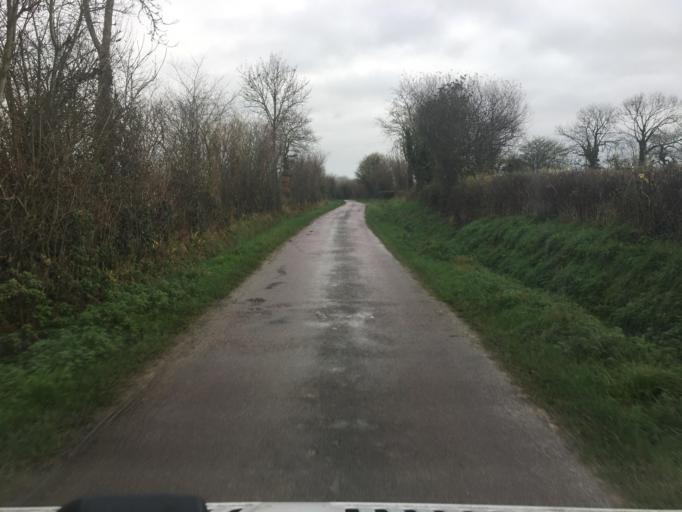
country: FR
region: Lower Normandy
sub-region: Departement de la Manche
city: Sainte-Mere-Eglise
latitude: 49.4229
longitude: -1.2711
